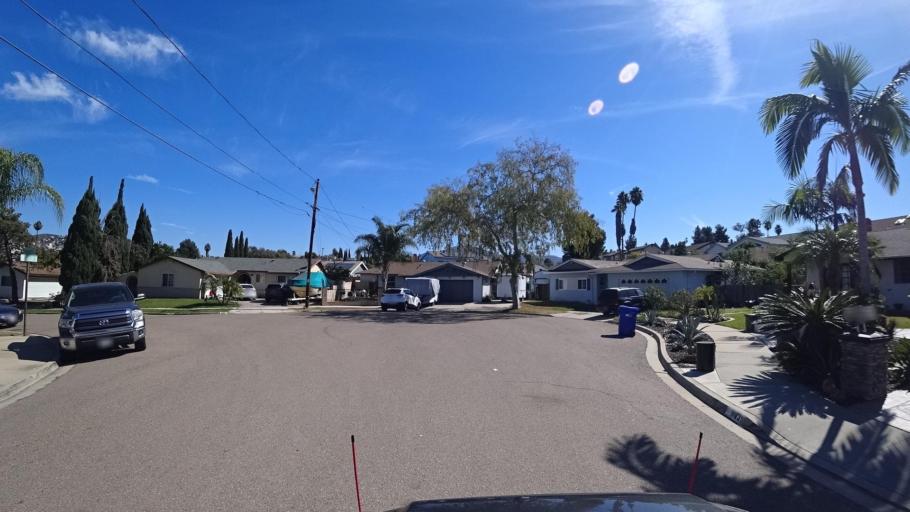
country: US
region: California
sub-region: San Diego County
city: La Presa
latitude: 32.7064
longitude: -117.0047
